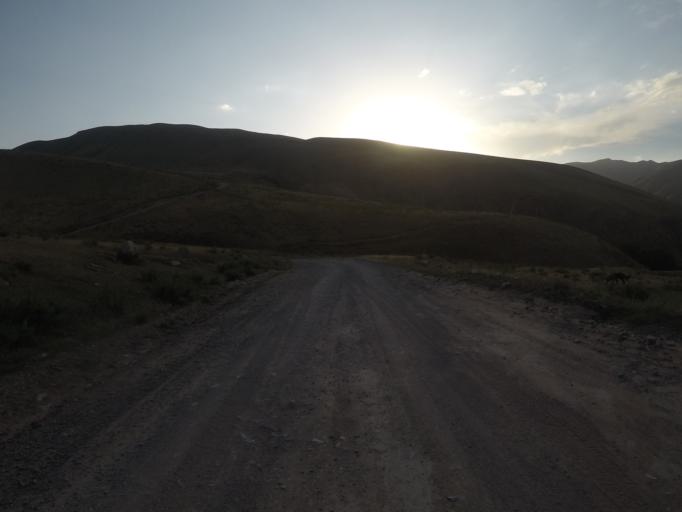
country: KG
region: Chuy
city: Bishkek
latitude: 42.6606
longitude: 74.6512
